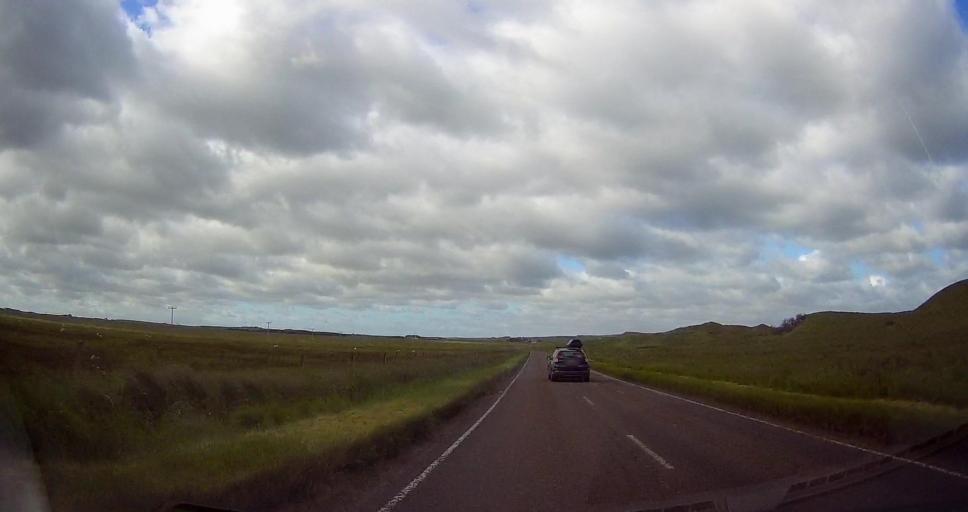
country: GB
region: Scotland
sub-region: Highland
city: Thurso
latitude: 58.6063
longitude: -3.3457
